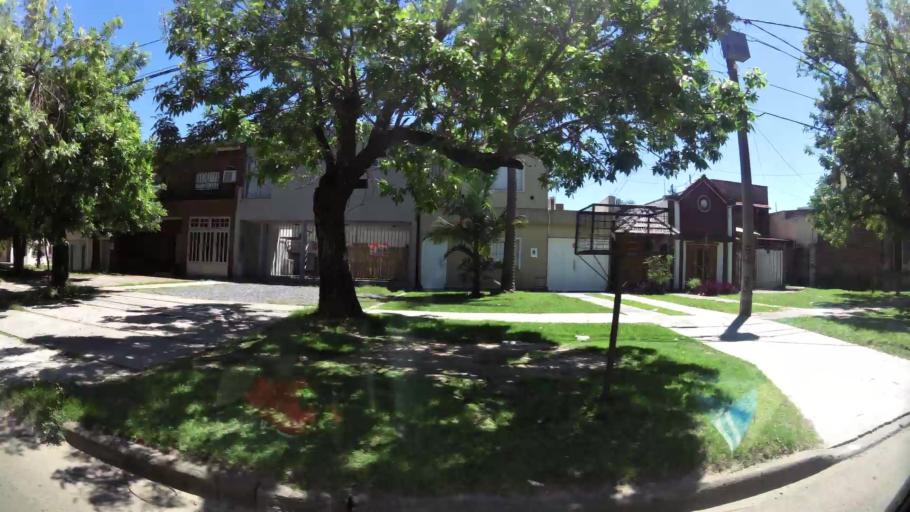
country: AR
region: Santa Fe
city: Santa Fe de la Vera Cruz
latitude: -31.6273
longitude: -60.7101
